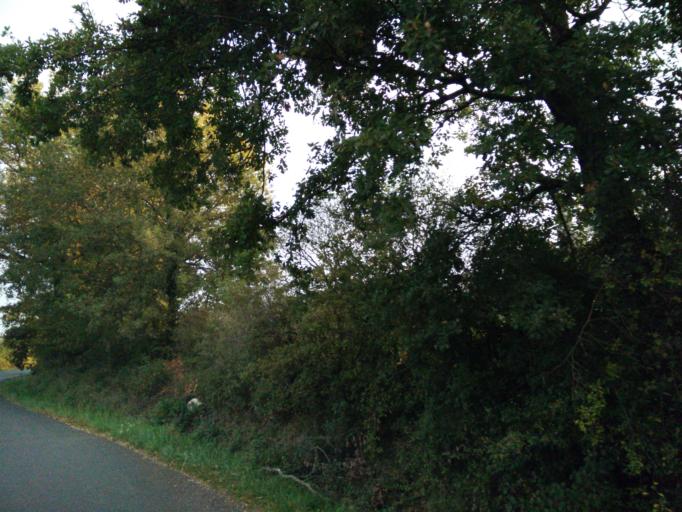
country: FR
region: Aquitaine
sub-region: Departement de la Dordogne
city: Rouffignac-Saint-Cernin-de-Reilhac
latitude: 45.0091
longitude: 0.9557
